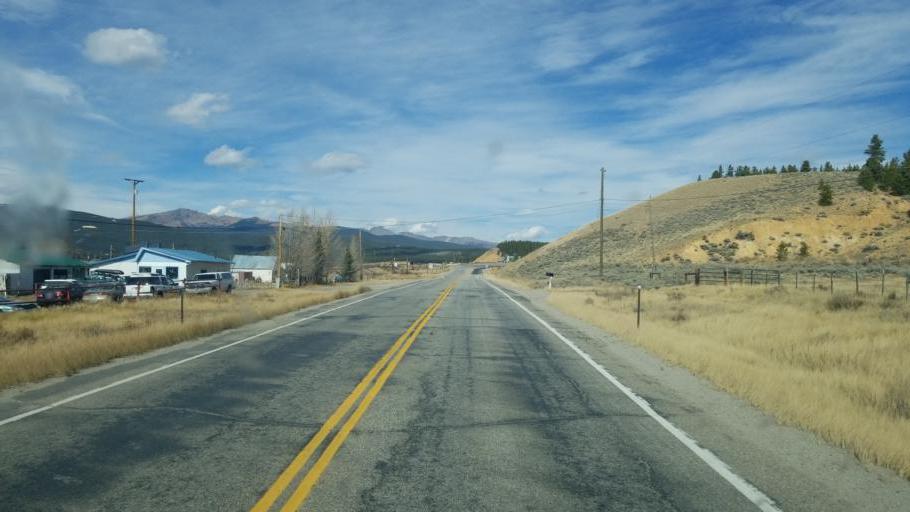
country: US
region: Colorado
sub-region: Lake County
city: Leadville North
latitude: 39.2172
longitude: -106.3475
